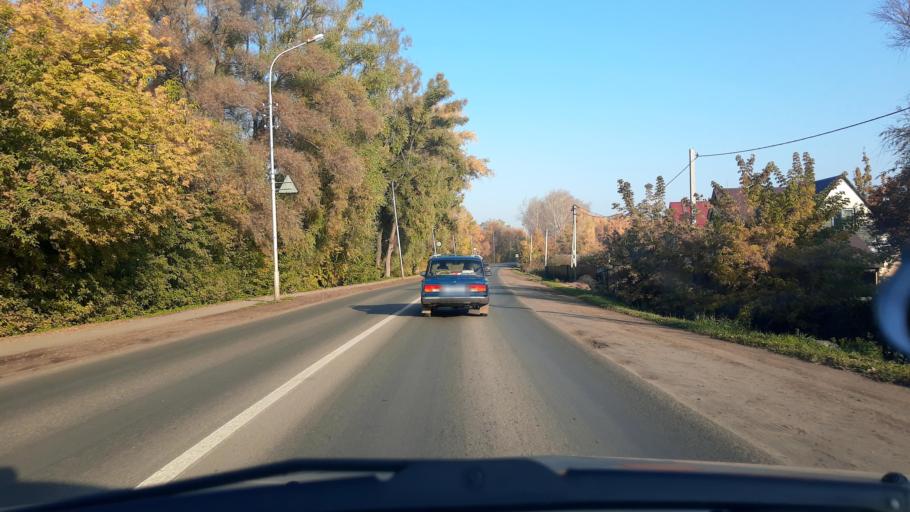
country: RU
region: Bashkortostan
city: Avdon
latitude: 54.7132
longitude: 55.8114
